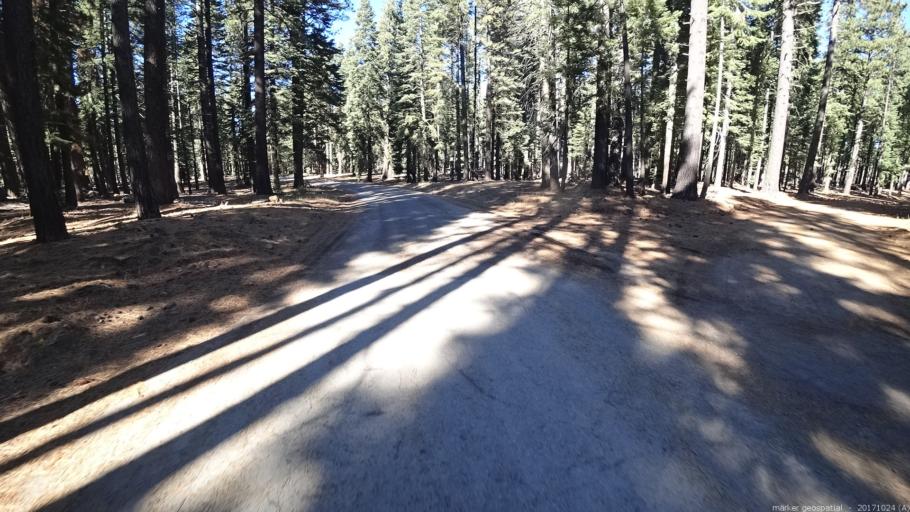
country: US
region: California
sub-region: Shasta County
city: Burney
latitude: 40.5917
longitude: -121.5423
